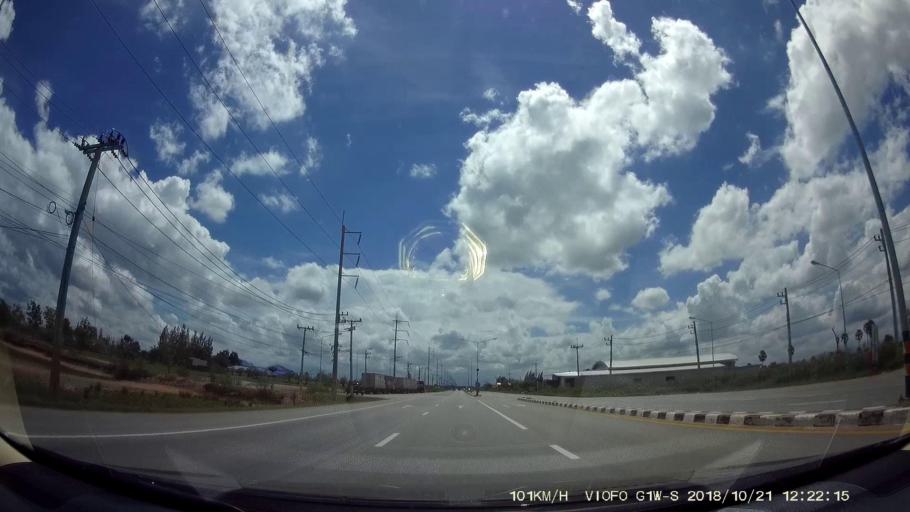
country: TH
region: Nakhon Ratchasima
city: Dan Khun Thot
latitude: 15.2642
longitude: 101.7898
